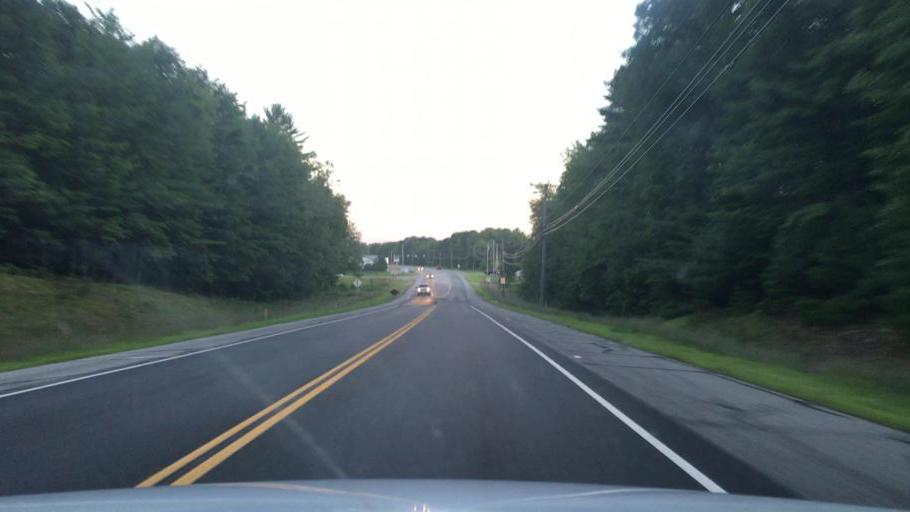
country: US
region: Maine
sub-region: Androscoggin County
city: Turner
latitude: 44.2059
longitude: -70.2458
